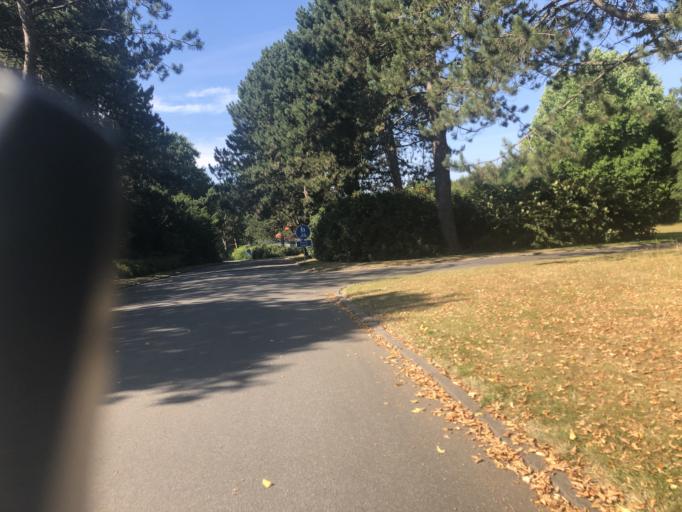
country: DK
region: Capital Region
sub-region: Gladsaxe Municipality
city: Buddinge
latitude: 55.7388
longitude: 12.4711
